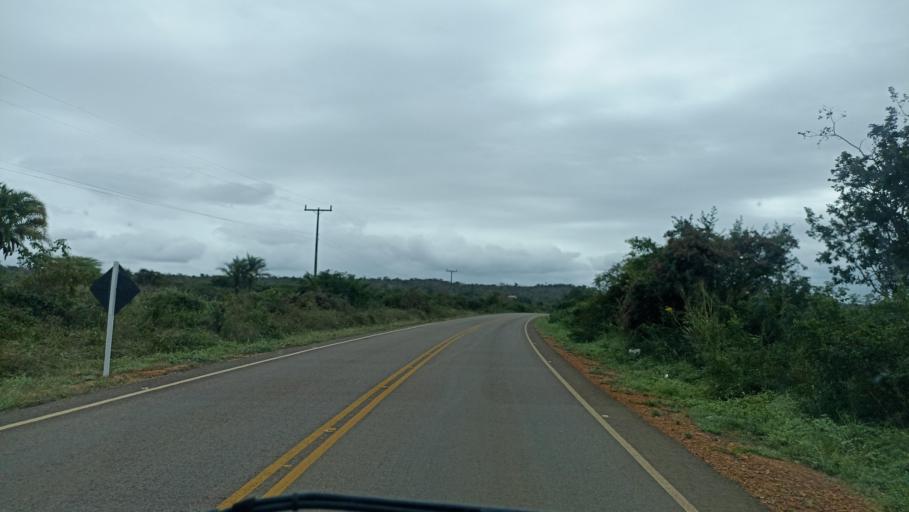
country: BR
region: Bahia
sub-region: Andarai
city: Vera Cruz
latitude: -13.0041
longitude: -40.9861
